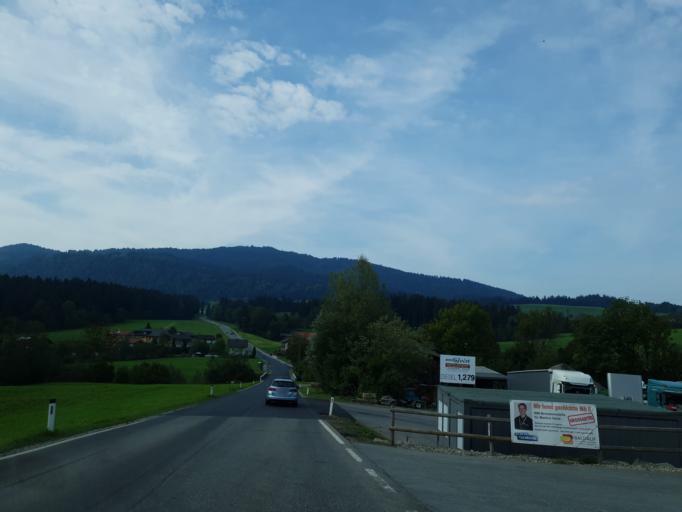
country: AT
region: Vorarlberg
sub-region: Politischer Bezirk Bregenz
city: Doren
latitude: 47.5147
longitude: 9.8649
